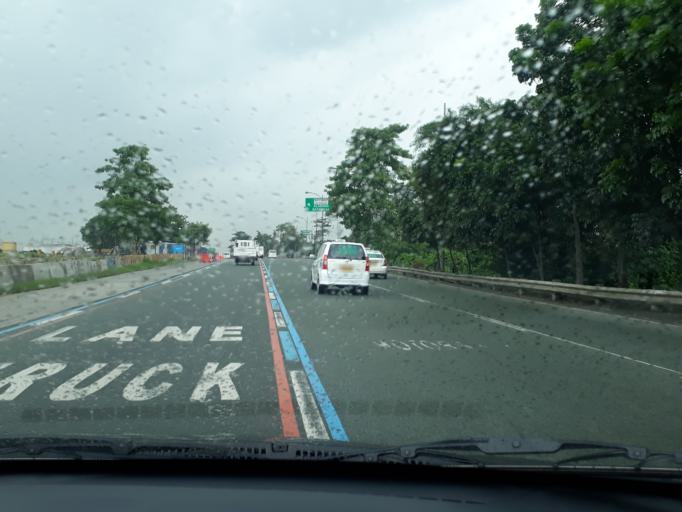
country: PH
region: Metro Manila
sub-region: Makati City
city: Makati City
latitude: 14.5162
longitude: 121.0396
